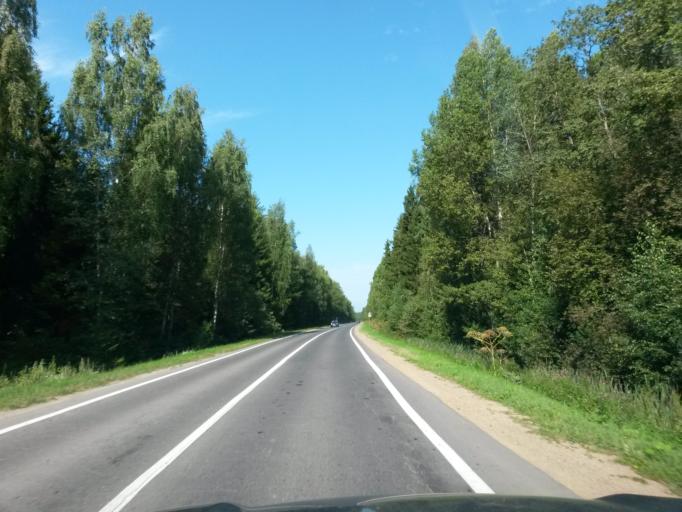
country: RU
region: Jaroslavl
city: Yaroslavl
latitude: 57.7999
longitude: 39.7988
